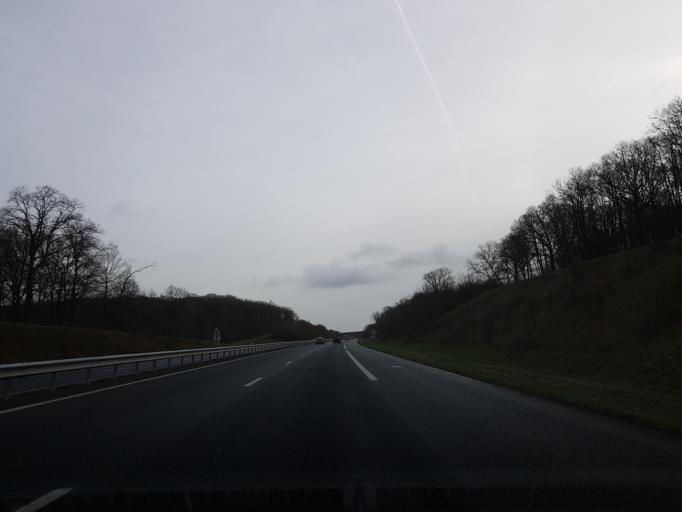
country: FR
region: Bourgogne
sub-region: Departement de l'Yonne
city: Soucy
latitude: 48.2421
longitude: 3.3637
